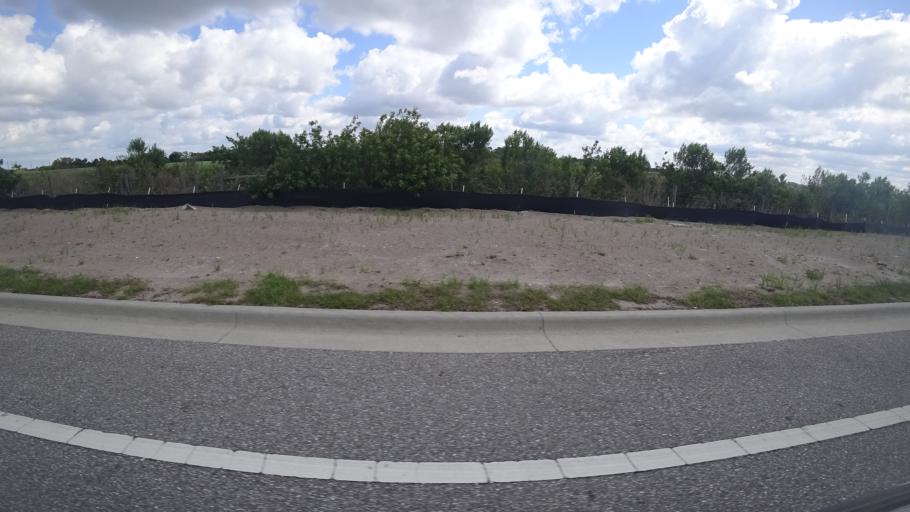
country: US
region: Florida
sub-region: Manatee County
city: Bayshore Gardens
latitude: 27.4366
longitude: -82.6233
